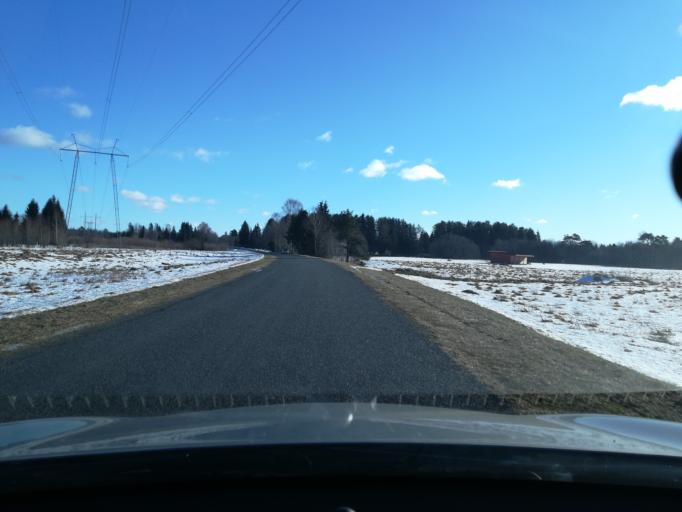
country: EE
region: Raplamaa
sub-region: Kohila vald
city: Kohila
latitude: 59.2352
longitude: 24.7593
